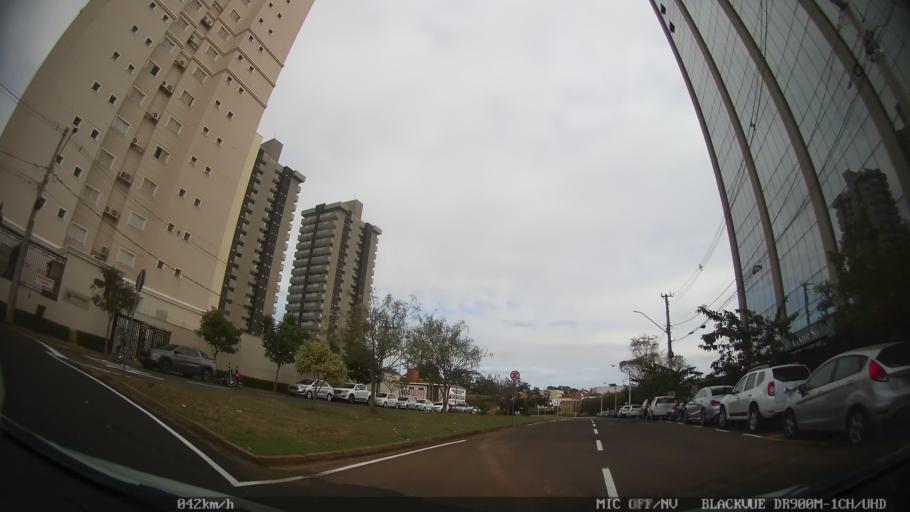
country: BR
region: Sao Paulo
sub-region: Sao Jose Do Rio Preto
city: Sao Jose do Rio Preto
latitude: -20.8300
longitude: -49.4077
